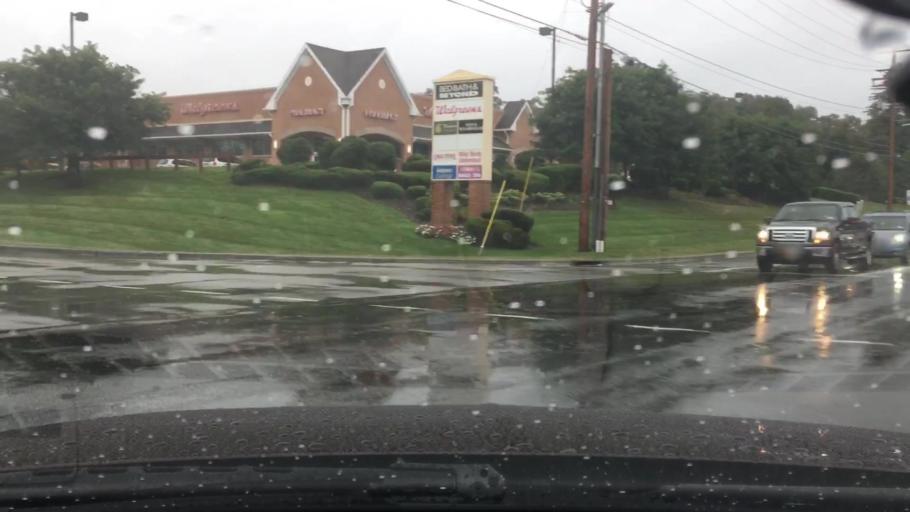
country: US
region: New York
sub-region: Dutchess County
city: Crown Heights
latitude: 41.6283
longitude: -73.9163
